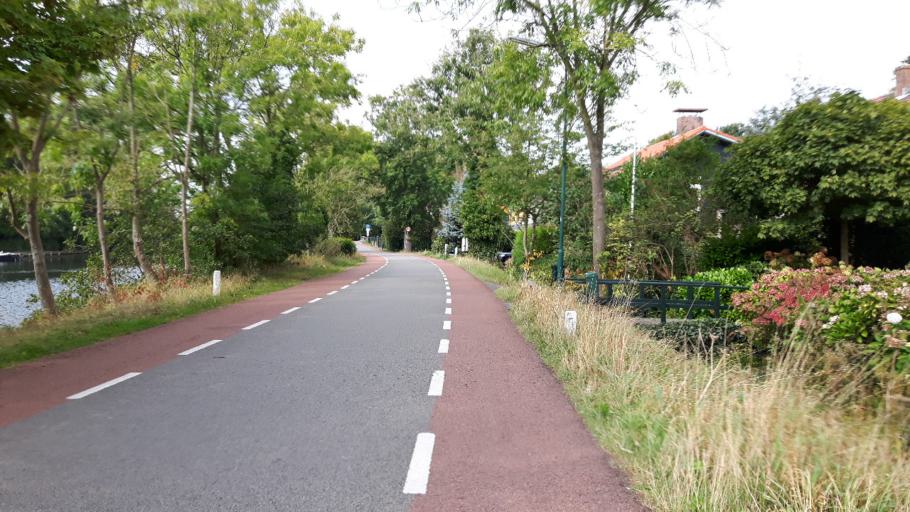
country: NL
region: Utrecht
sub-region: Stichtse Vecht
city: Spechtenkamp
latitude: 52.1580
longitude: 5.0199
